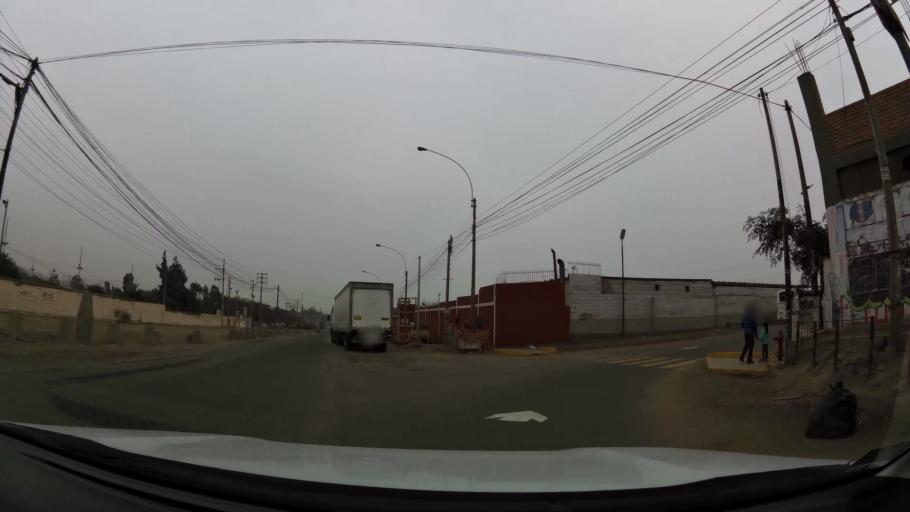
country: PE
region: Lima
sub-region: Lima
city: Surco
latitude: -12.1732
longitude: -76.9767
